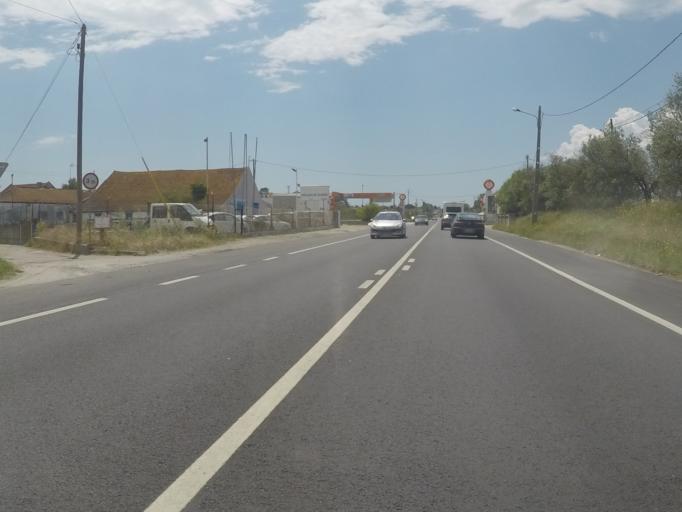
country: PT
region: Setubal
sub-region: Setubal
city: Setubal
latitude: 38.5505
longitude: -8.8104
